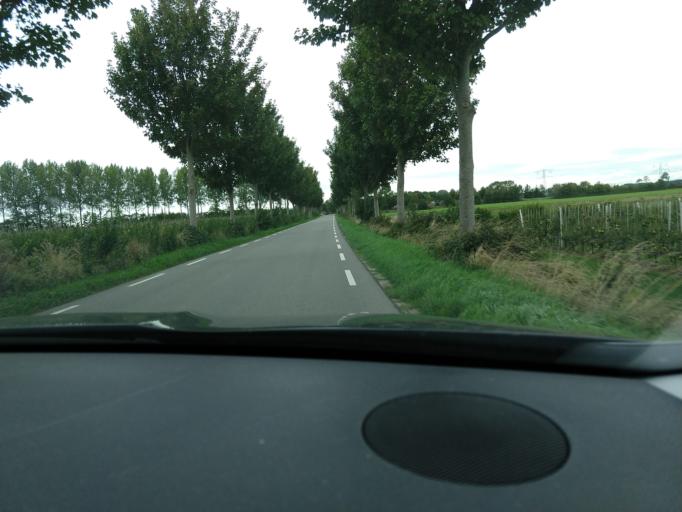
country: NL
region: Zeeland
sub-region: Gemeente Goes
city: Goes
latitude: 51.4234
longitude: 3.8809
